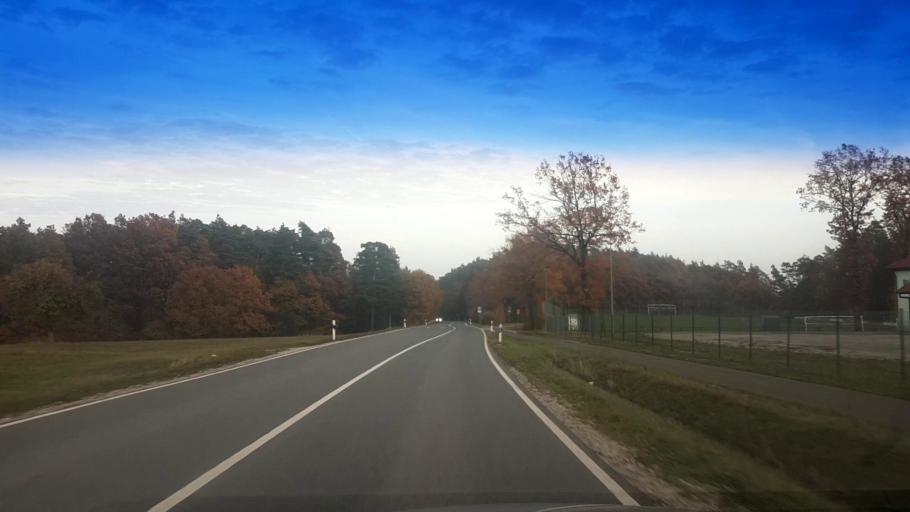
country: DE
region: Bavaria
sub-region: Upper Franconia
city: Viereth-Trunstadt
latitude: 49.9032
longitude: 10.7832
